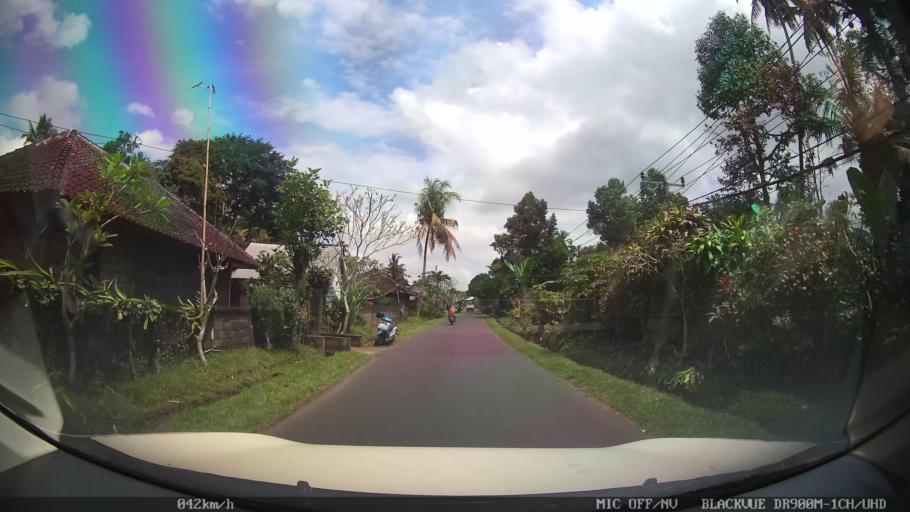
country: ID
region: Bali
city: Banjar Bebalang
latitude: -8.4796
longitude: 115.3704
